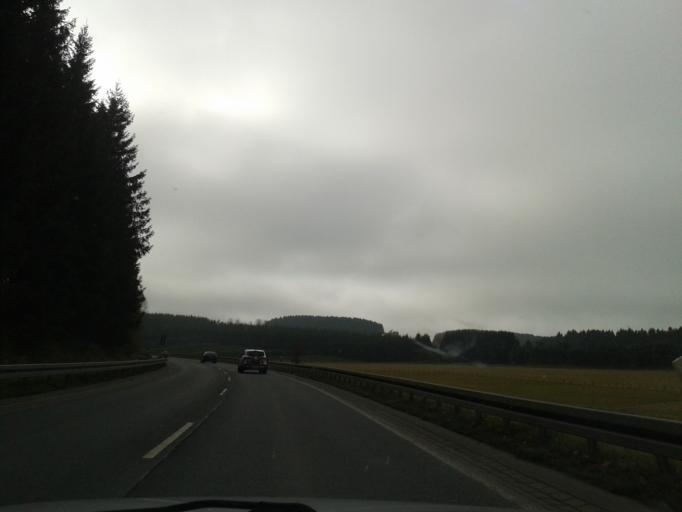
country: DE
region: North Rhine-Westphalia
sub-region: Regierungsbezirk Arnsberg
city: Winterberg
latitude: 51.2163
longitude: 8.5383
